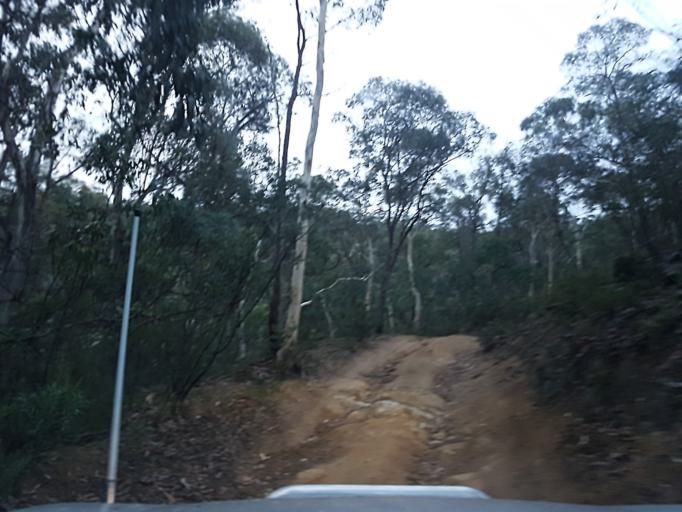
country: AU
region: New South Wales
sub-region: Snowy River
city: Jindabyne
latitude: -36.8646
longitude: 148.2353
